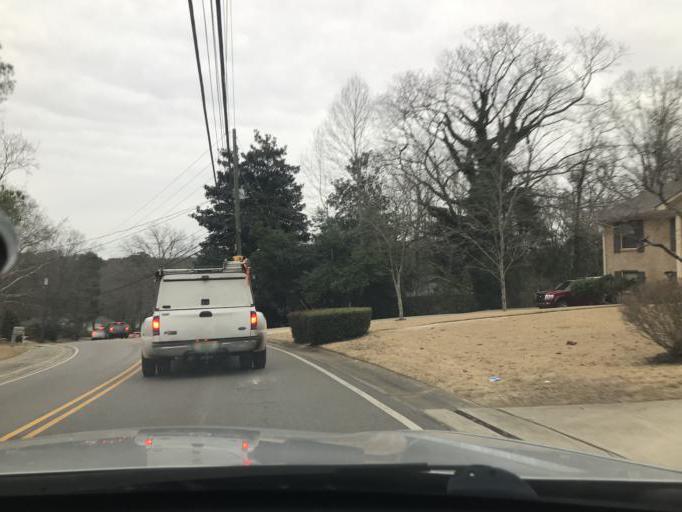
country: US
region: Alabama
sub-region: Jefferson County
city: Cahaba Heights
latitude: 33.4774
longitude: -86.7215
